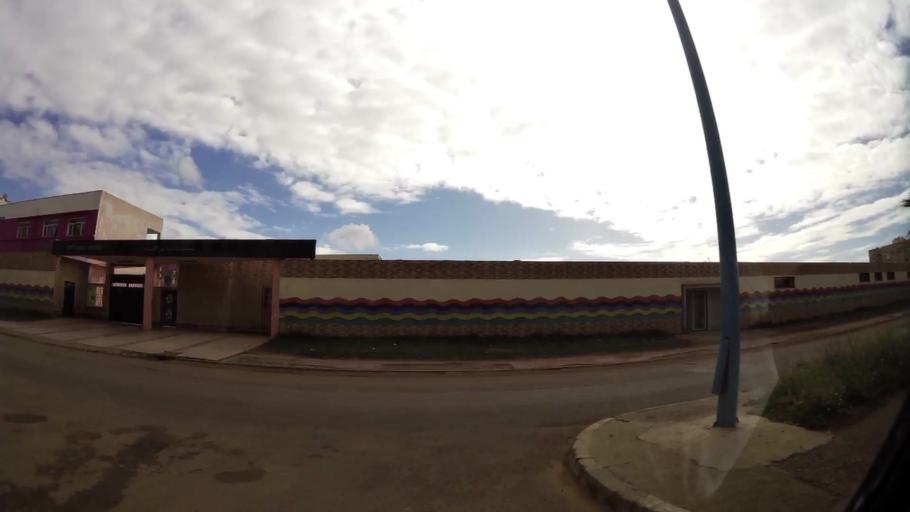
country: MA
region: Grand Casablanca
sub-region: Mohammedia
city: Mohammedia
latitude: 33.6853
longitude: -7.3741
